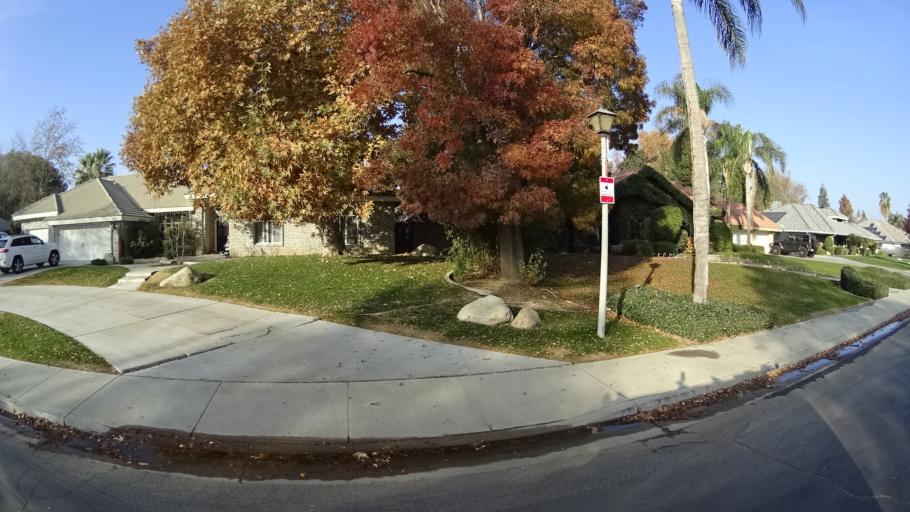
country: US
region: California
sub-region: Kern County
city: Rosedale
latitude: 35.3740
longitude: -119.1311
